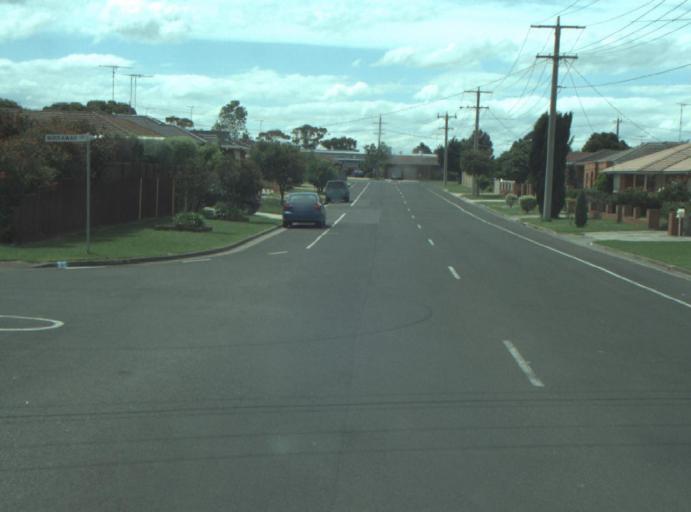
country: AU
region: Victoria
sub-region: Greater Geelong
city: Bell Park
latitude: -38.0917
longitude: 144.3414
